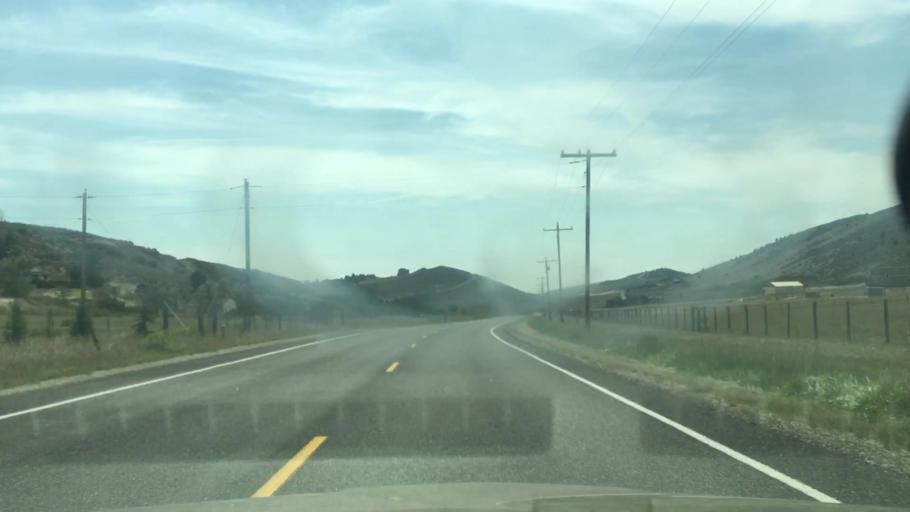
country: US
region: Colorado
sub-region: Larimer County
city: Campion
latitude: 40.3459
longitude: -105.1840
